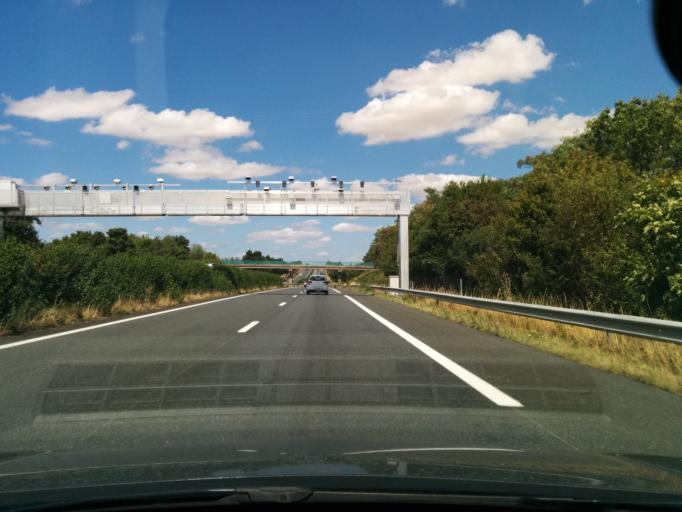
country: FR
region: Centre
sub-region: Departement de l'Indre
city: Vatan
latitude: 46.9772
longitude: 1.7670
